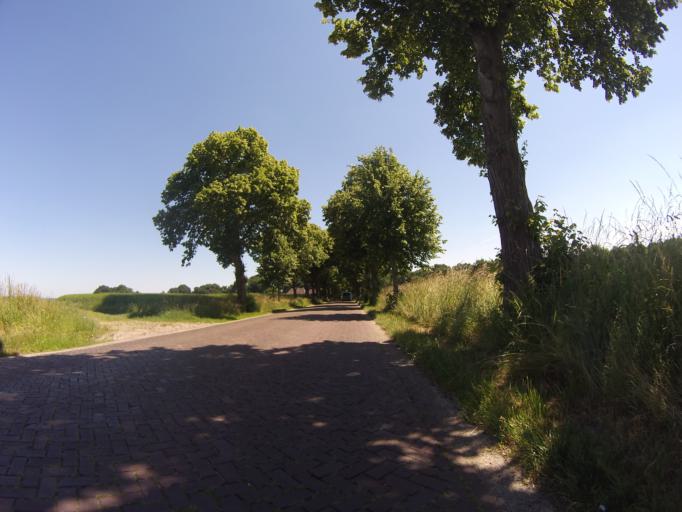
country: NL
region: Drenthe
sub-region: Gemeente Emmen
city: Emmen
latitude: 52.8127
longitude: 6.9297
